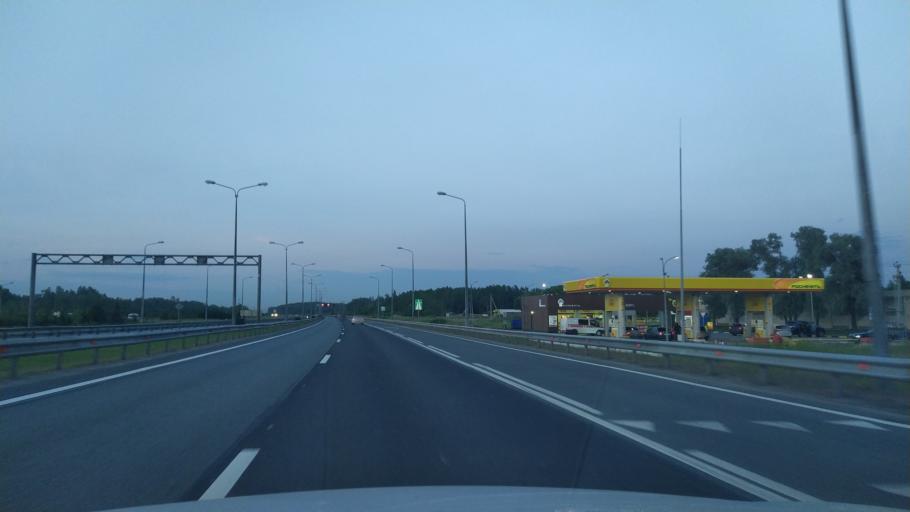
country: RU
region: St.-Petersburg
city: Aleksandrovskaya
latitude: 60.0389
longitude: 29.9985
